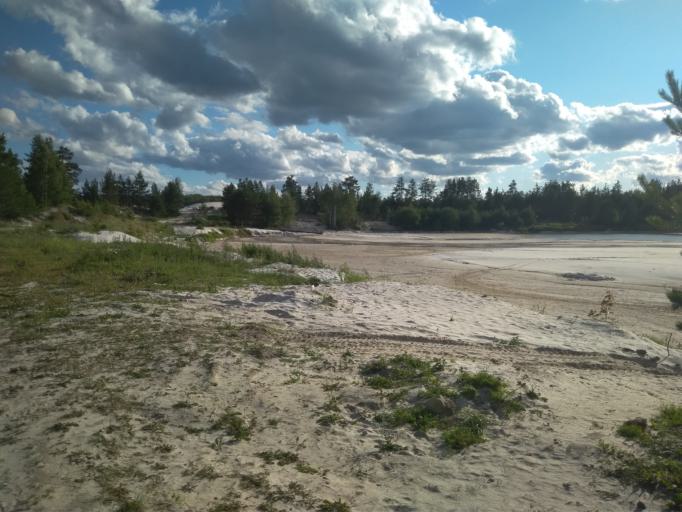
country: RU
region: Ulyanovsk
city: Silikatnyy
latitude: 53.9824
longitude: 48.3342
